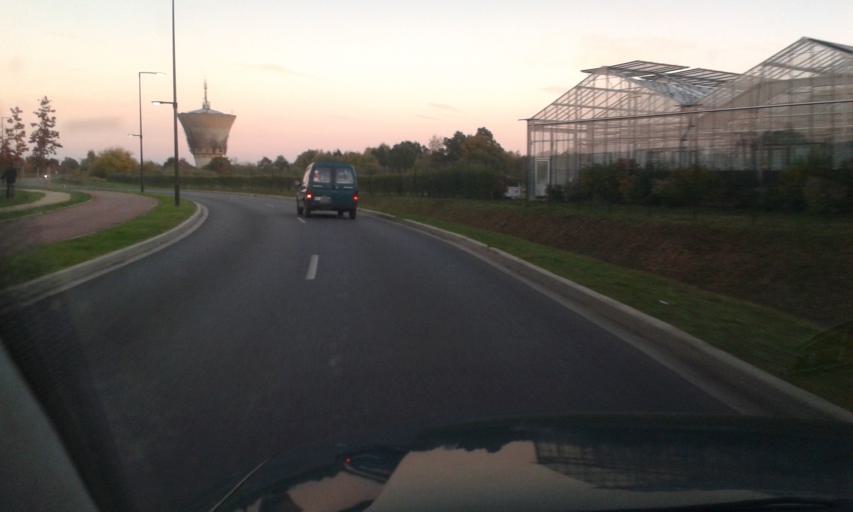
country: FR
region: Centre
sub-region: Departement du Loiret
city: Olivet
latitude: 47.8591
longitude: 1.8871
